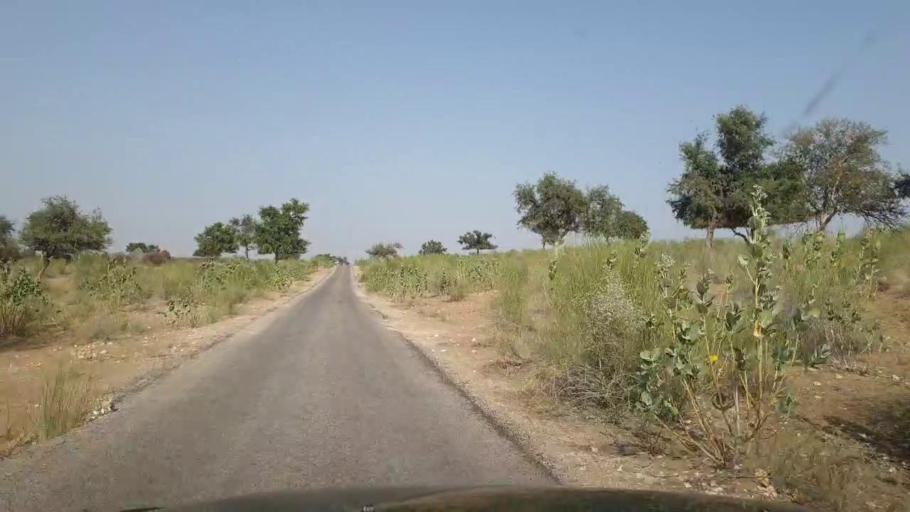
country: PK
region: Sindh
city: Islamkot
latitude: 25.1112
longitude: 70.4266
